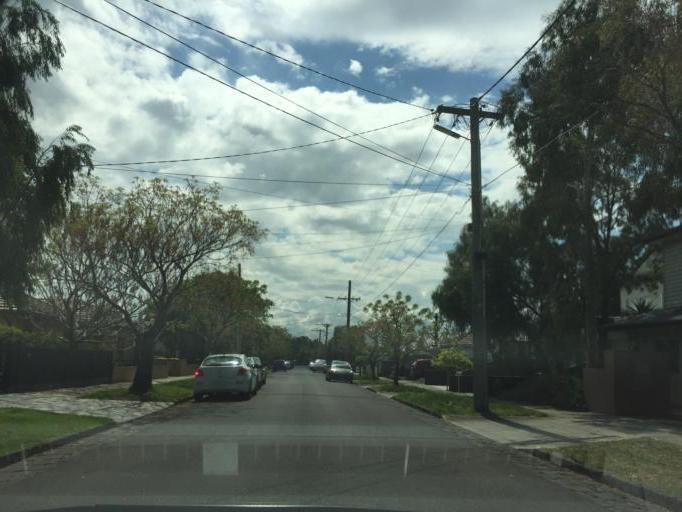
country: AU
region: Victoria
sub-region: Maribyrnong
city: West Footscray
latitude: -37.7922
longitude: 144.8805
